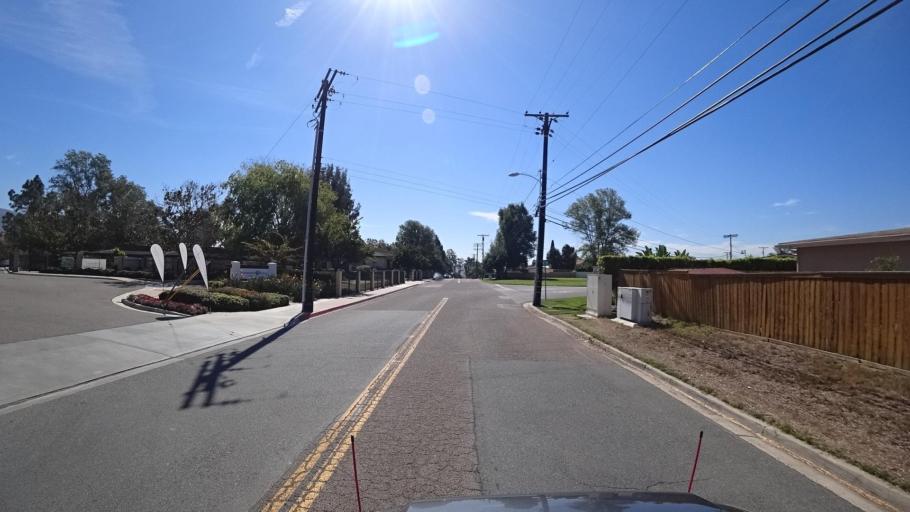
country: US
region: California
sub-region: San Diego County
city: La Presa
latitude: 32.7028
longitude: -117.0020
